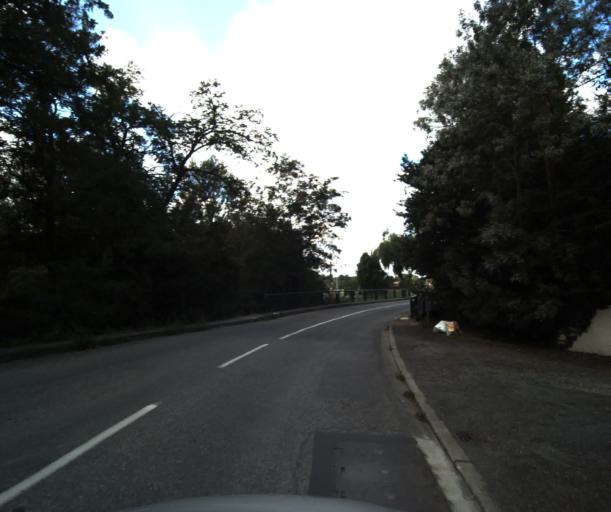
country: FR
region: Midi-Pyrenees
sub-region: Departement de la Haute-Garonne
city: Lacasse
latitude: 43.3963
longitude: 1.2562
